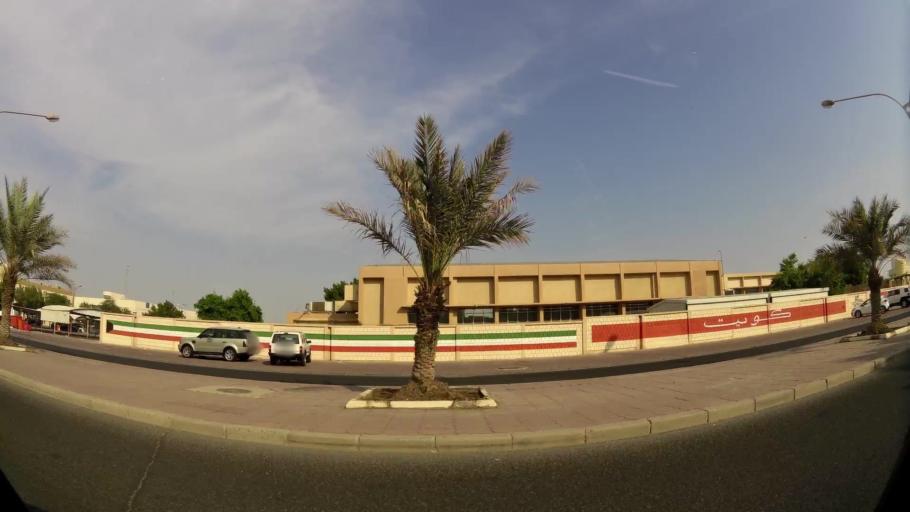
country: KW
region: Al Asimah
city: Ash Shamiyah
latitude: 29.3114
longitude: 47.9841
